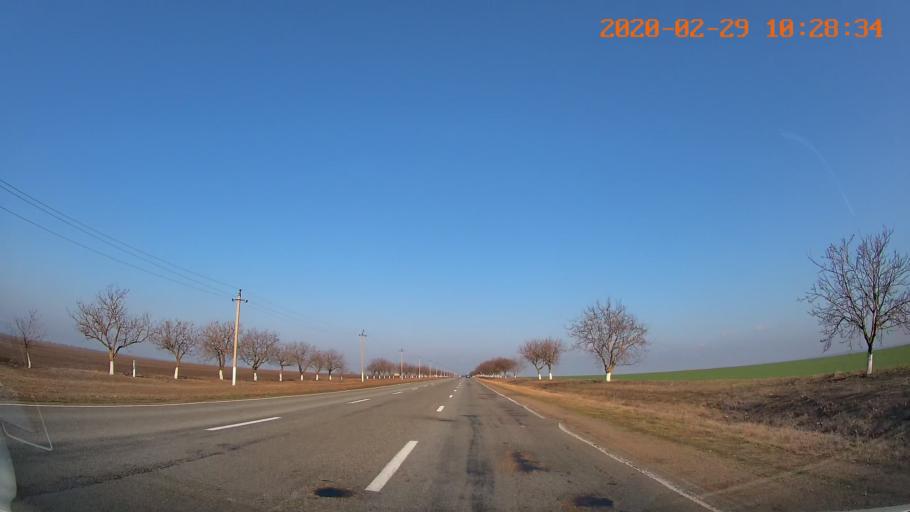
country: MD
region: Telenesti
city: Tiraspolul Nou
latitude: 46.9124
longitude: 29.5906
